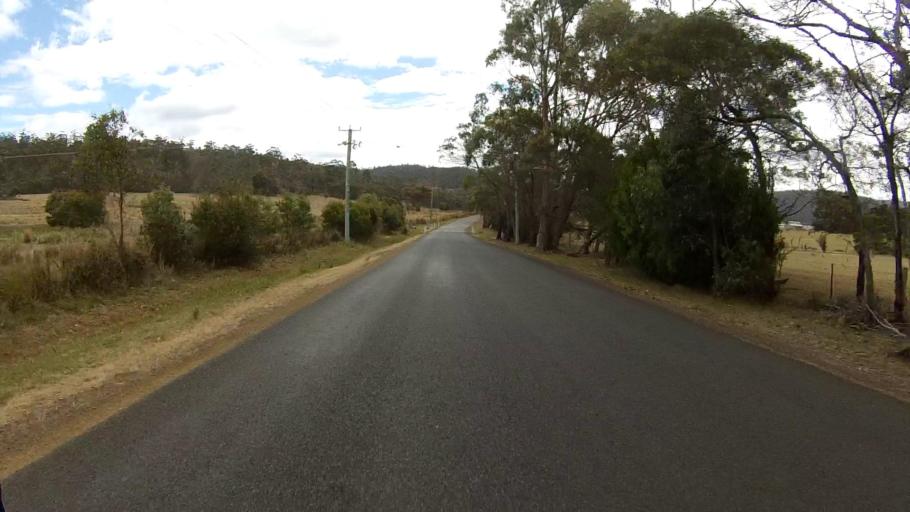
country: AU
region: Tasmania
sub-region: Sorell
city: Sorell
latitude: -42.5722
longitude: 147.8883
